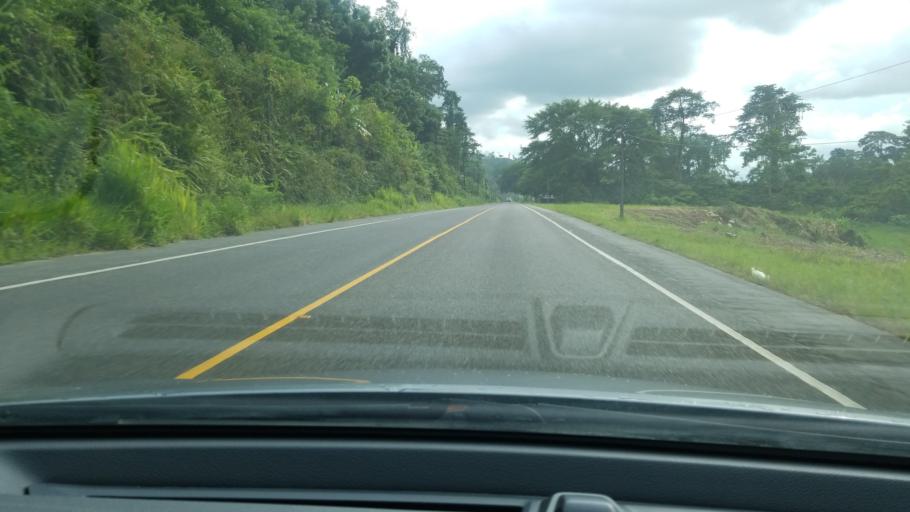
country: HN
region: Cortes
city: Potrerillos
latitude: 15.5956
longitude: -88.3018
